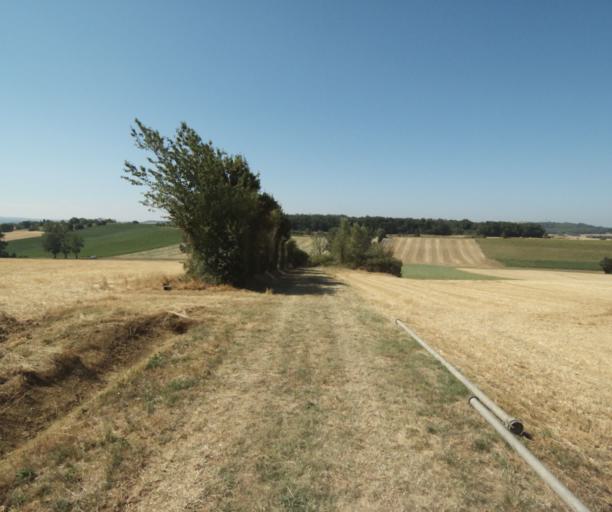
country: FR
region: Midi-Pyrenees
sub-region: Departement de la Haute-Garonne
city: Saint-Felix-Lauragais
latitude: 43.5026
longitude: 1.9279
